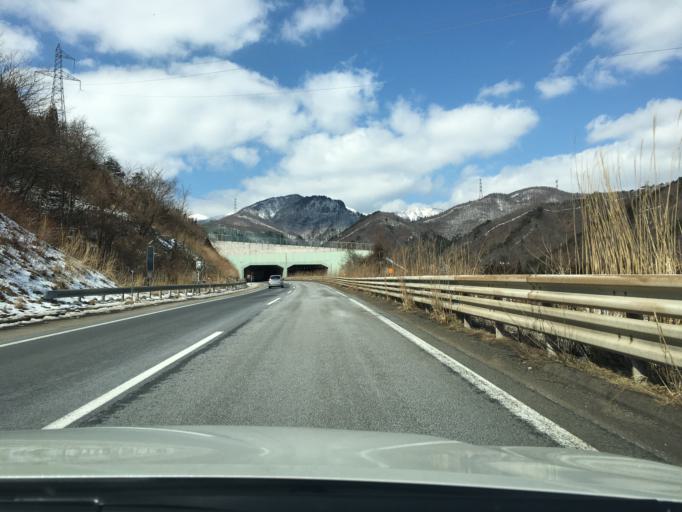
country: JP
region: Yamagata
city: Yamagata-shi
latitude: 38.2182
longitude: 140.5198
